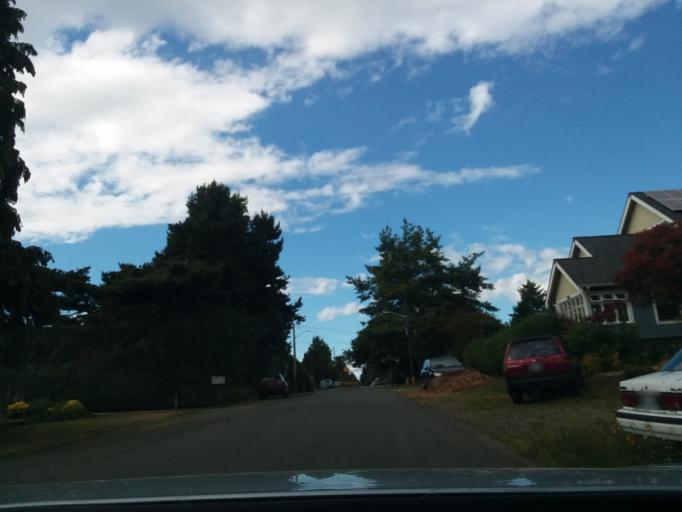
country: US
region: Washington
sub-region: King County
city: Shoreline
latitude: 47.6954
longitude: -122.3527
